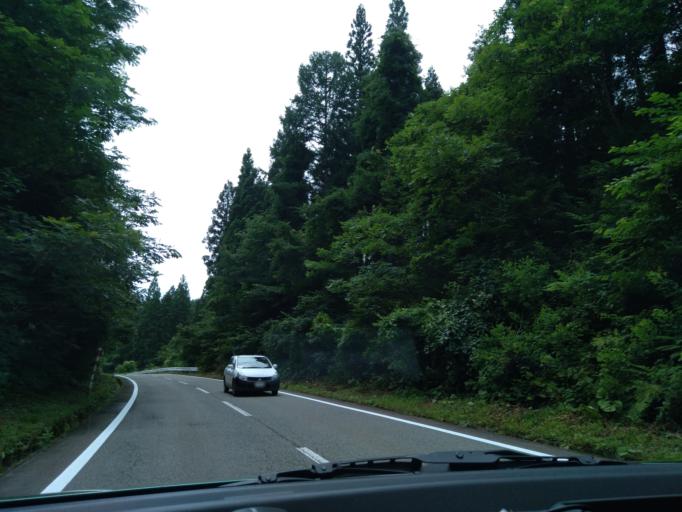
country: JP
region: Akita
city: Kakunodatemachi
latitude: 39.5597
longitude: 140.6328
